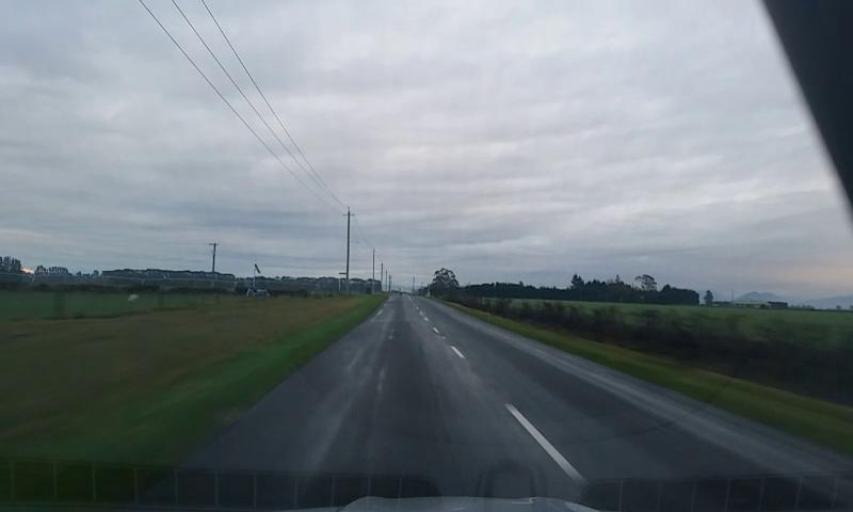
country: NZ
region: Canterbury
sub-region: Ashburton District
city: Rakaia
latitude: -43.7529
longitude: 171.8685
